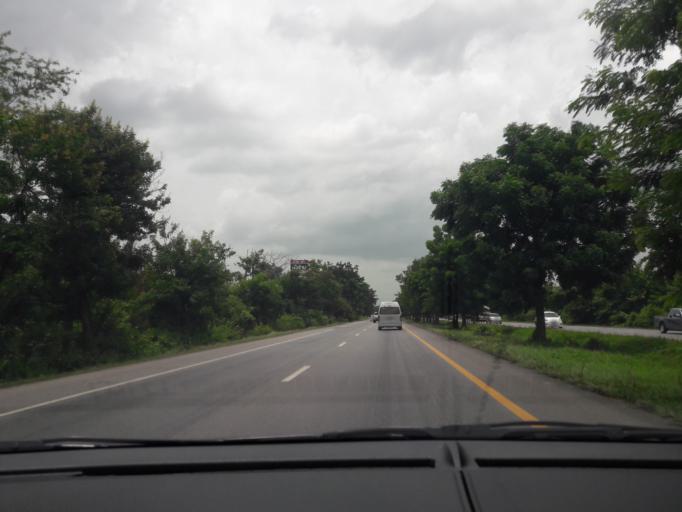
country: TH
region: Nakhon Ratchasima
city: Chaloem Phra Kiat
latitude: 15.0797
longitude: 102.2255
